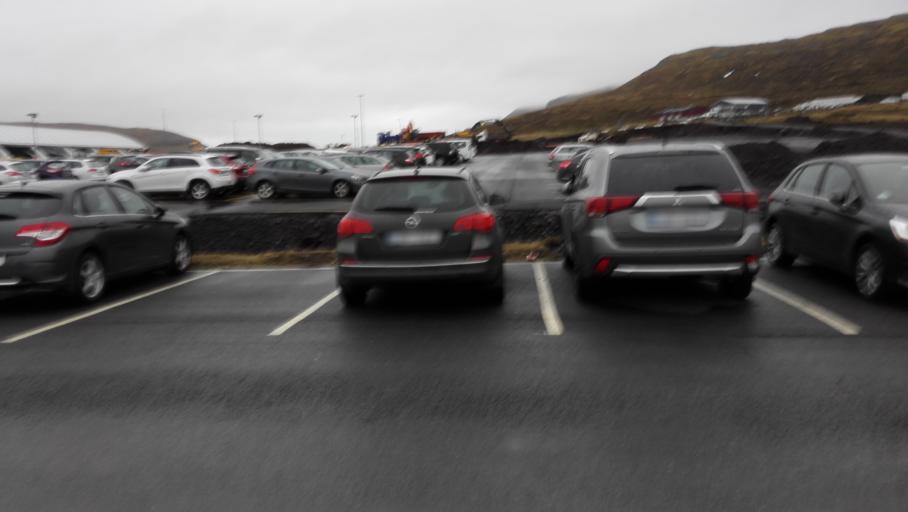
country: FO
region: Vagar
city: Midvagur
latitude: 62.0676
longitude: -7.2763
